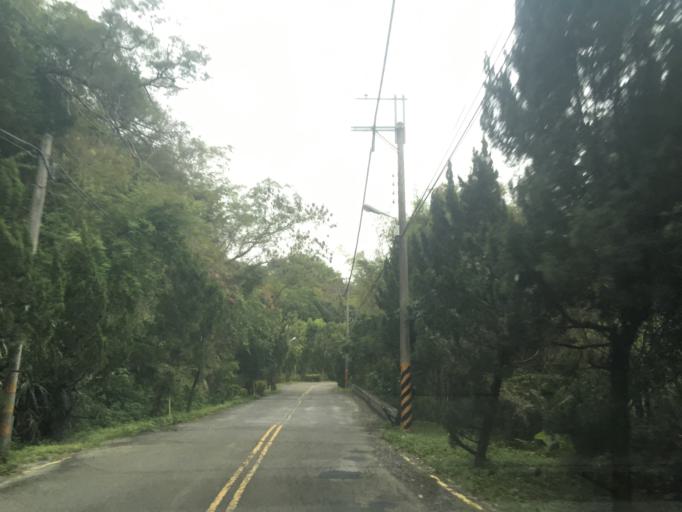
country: TW
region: Taiwan
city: Zhongxing New Village
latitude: 24.0347
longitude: 120.7425
